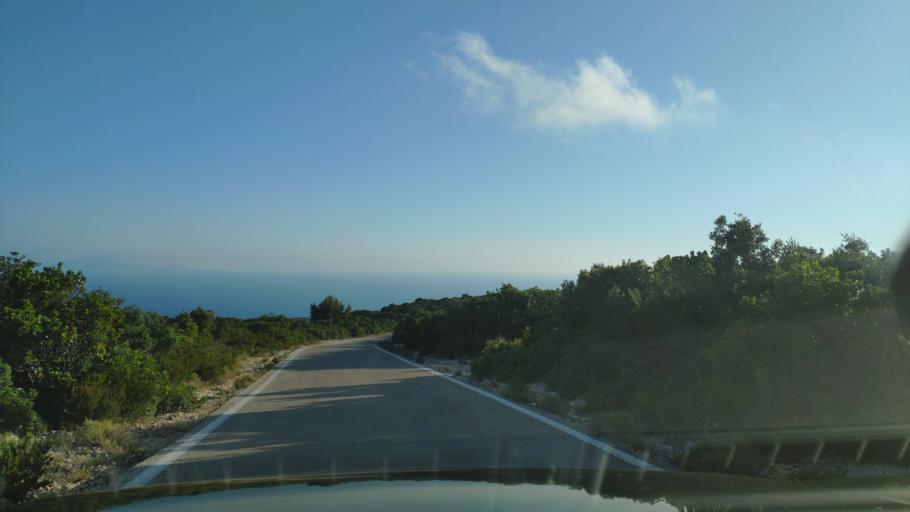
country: GR
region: Ionian Islands
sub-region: Lefkada
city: Nidri
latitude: 38.5992
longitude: 20.5580
